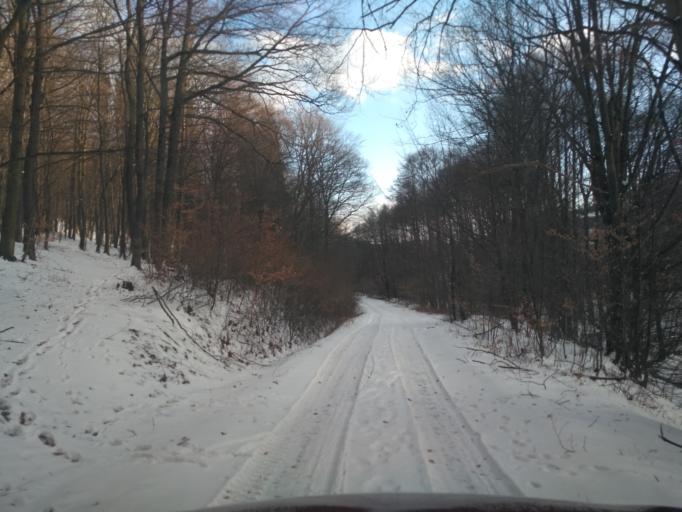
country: SK
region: Kosicky
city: Kosice
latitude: 48.7453
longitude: 21.1521
